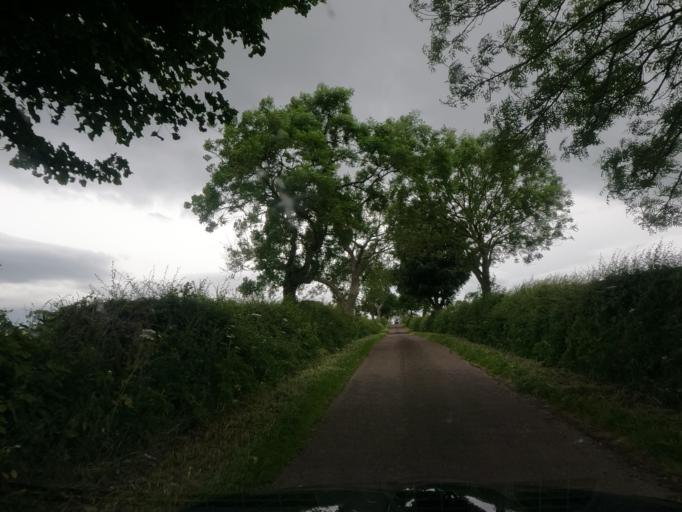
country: GB
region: England
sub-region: Northumberland
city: Lowick
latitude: 55.6117
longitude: -1.9617
